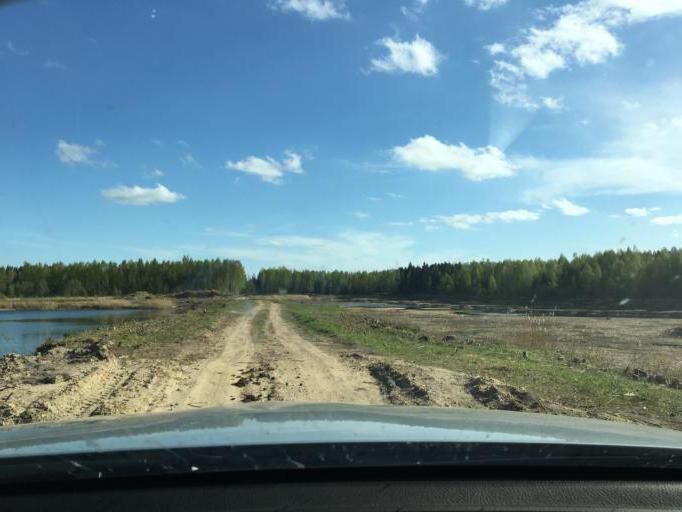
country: LV
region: Ozolnieku
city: Ozolnieki
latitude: 56.6660
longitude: 23.8652
